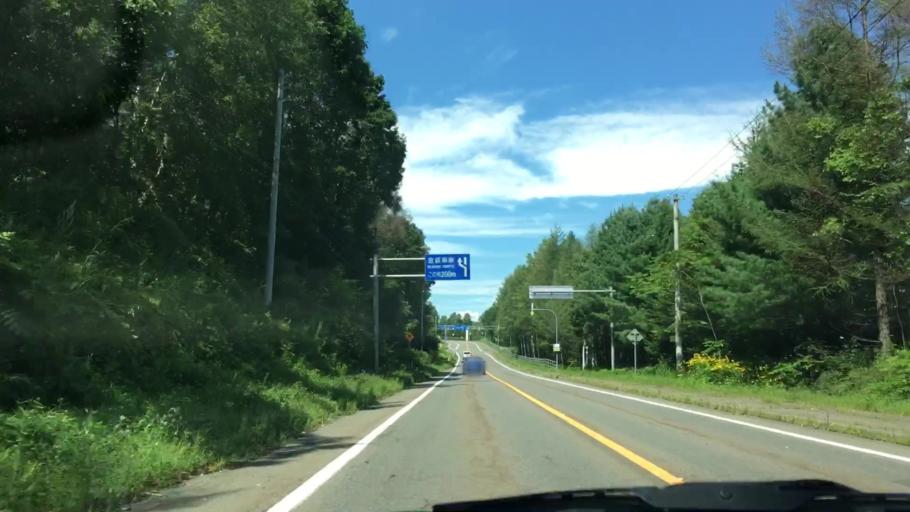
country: JP
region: Hokkaido
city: Otofuke
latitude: 43.2343
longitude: 143.5395
